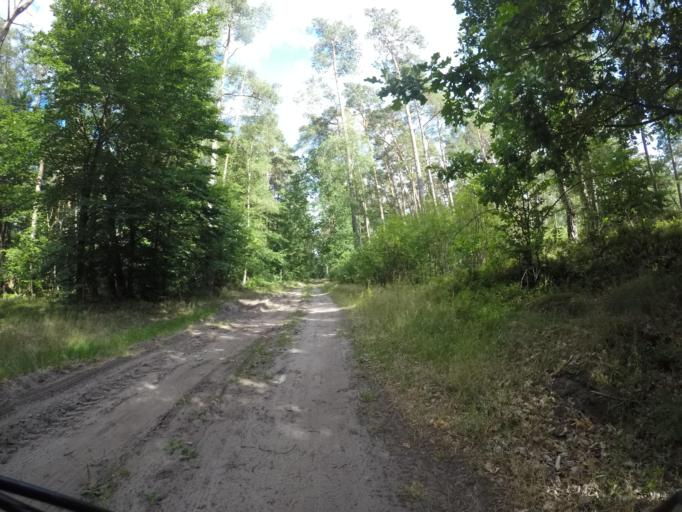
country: DE
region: Lower Saxony
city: Neu Darchau
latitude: 53.2707
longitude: 10.9790
